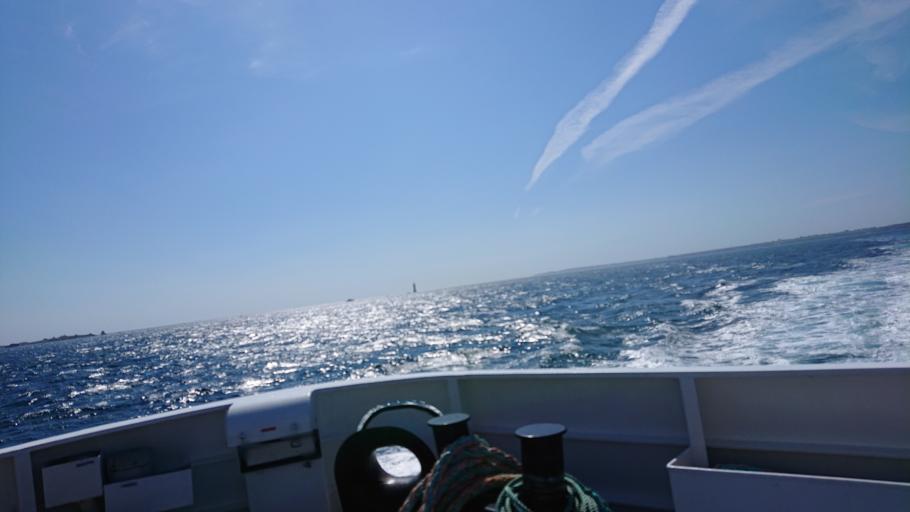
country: FR
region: Brittany
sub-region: Departement du Finistere
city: Lampaul-Plouarzel
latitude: 48.4446
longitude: -4.9918
